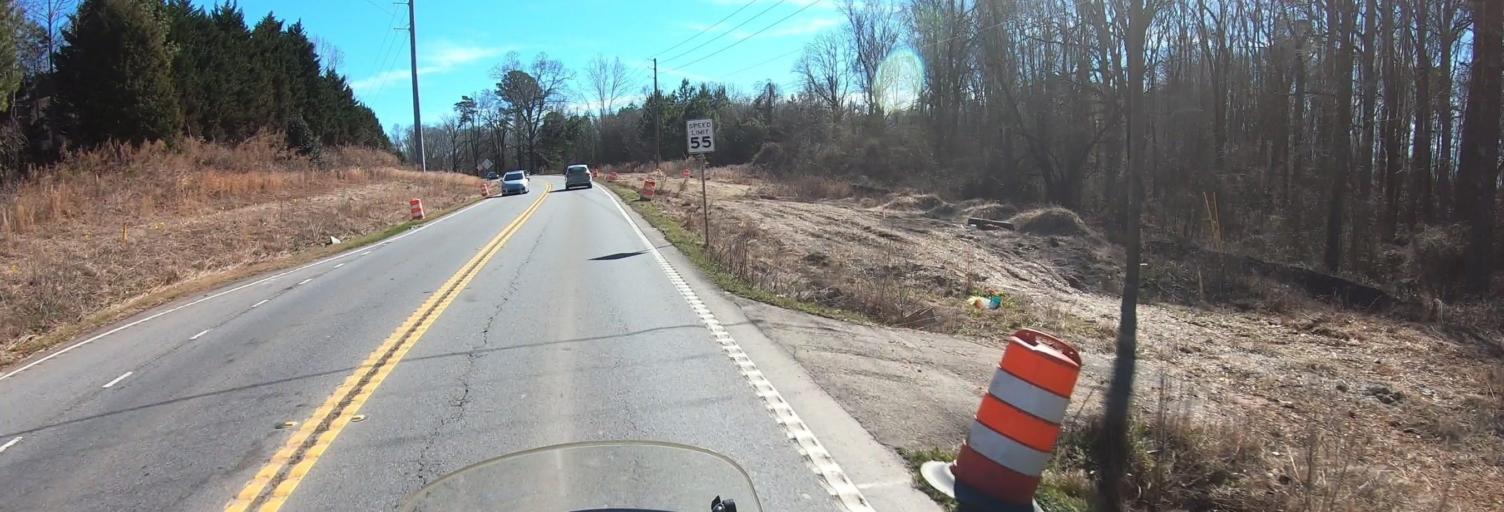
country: US
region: Georgia
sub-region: Forsyth County
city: Cumming
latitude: 34.2876
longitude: -84.1402
